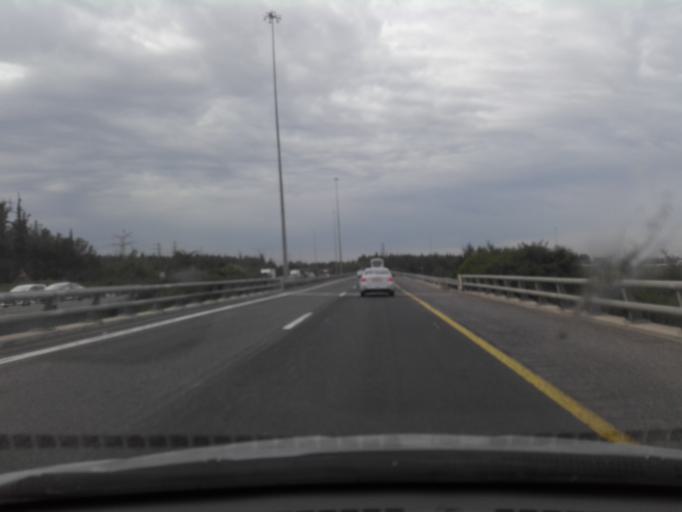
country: PS
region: West Bank
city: Budrus
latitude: 31.9619
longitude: 34.9420
